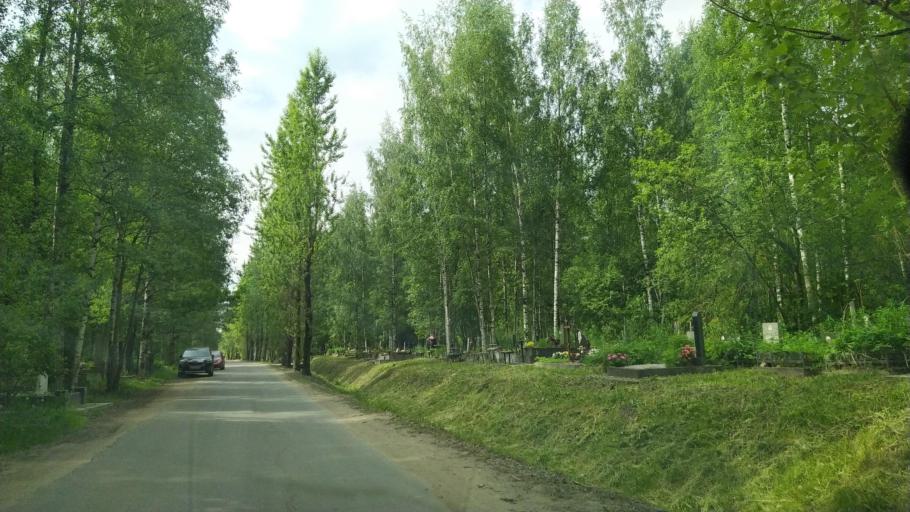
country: RU
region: St.-Petersburg
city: Dachnoye
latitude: 59.7704
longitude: 30.2651
